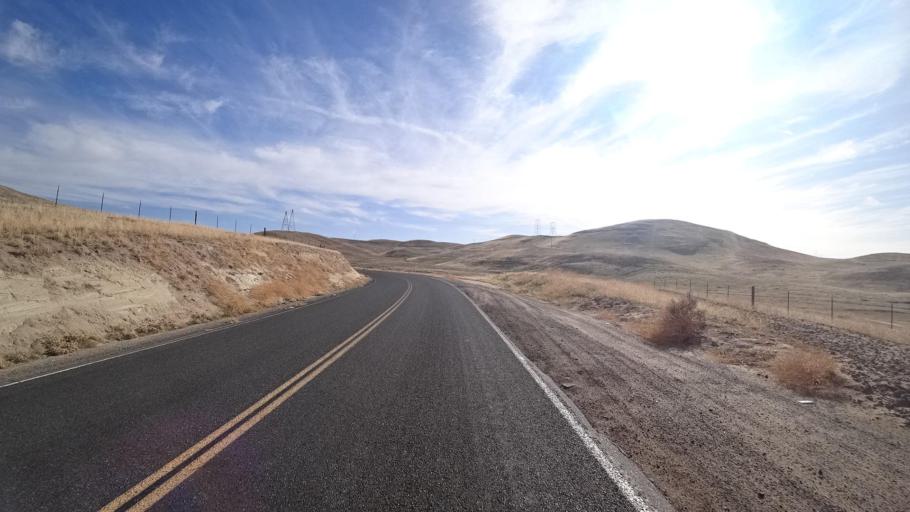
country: US
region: California
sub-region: Kern County
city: Oildale
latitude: 35.6094
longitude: -118.9239
